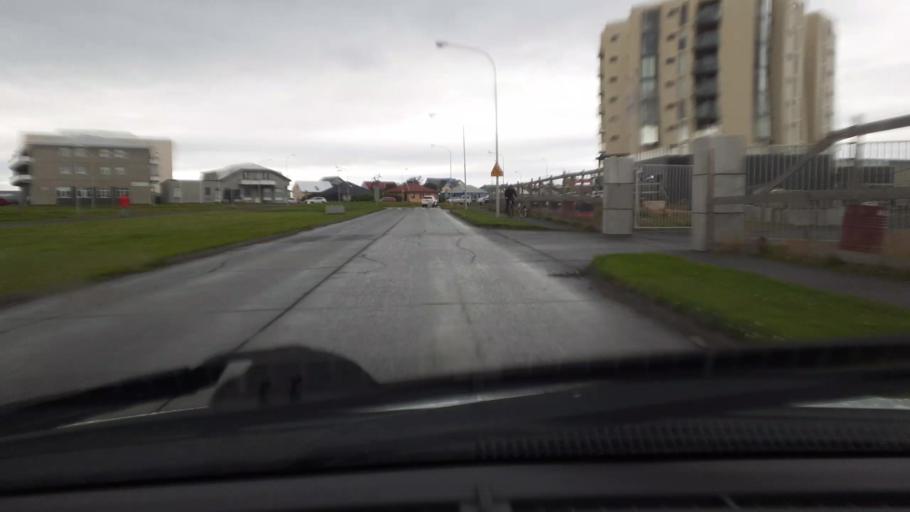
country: IS
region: West
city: Akranes
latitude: 64.3209
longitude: -22.0663
